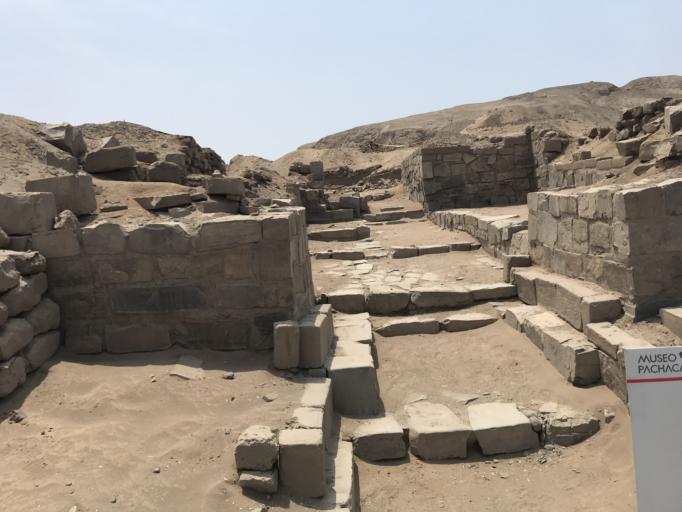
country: PE
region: Lima
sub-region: Lima
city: Punta Hermosa
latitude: -12.2591
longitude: -76.9003
